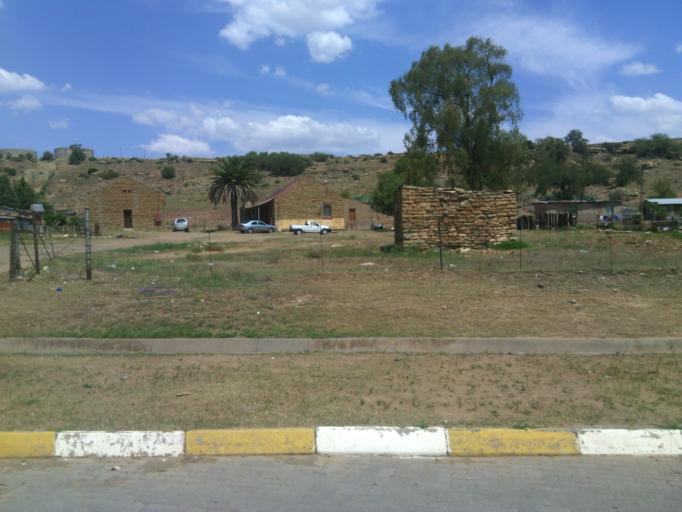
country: ZA
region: Orange Free State
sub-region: Xhariep District Municipality
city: Dewetsdorp
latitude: -29.5853
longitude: 26.6696
